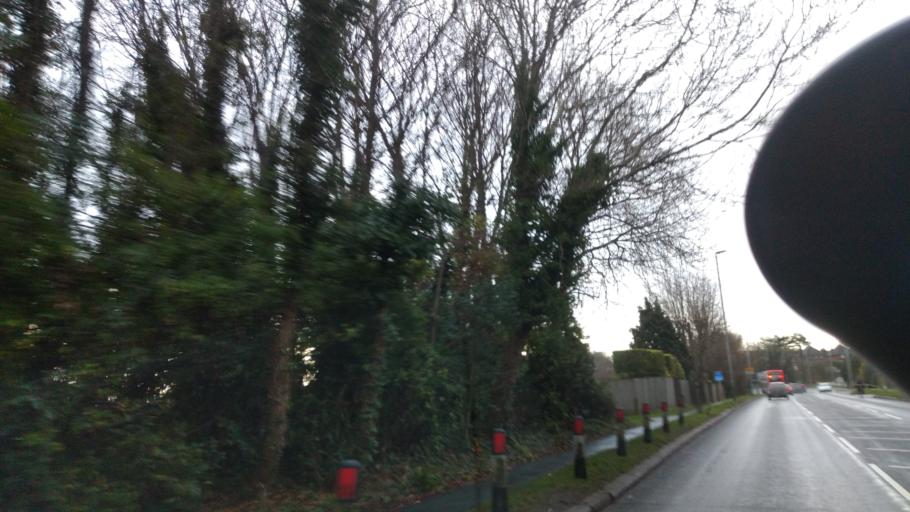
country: GB
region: England
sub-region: East Sussex
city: Eastbourne
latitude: 50.7909
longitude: 0.2567
